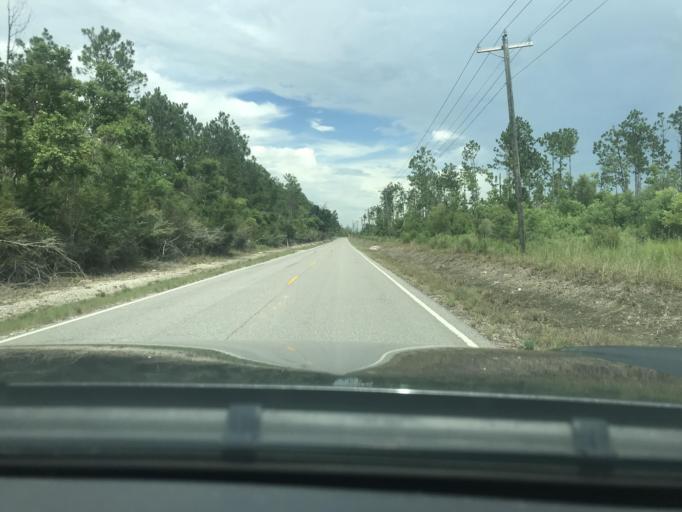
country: US
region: Louisiana
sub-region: Calcasieu Parish
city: Moss Bluff
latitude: 30.3885
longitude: -93.2380
